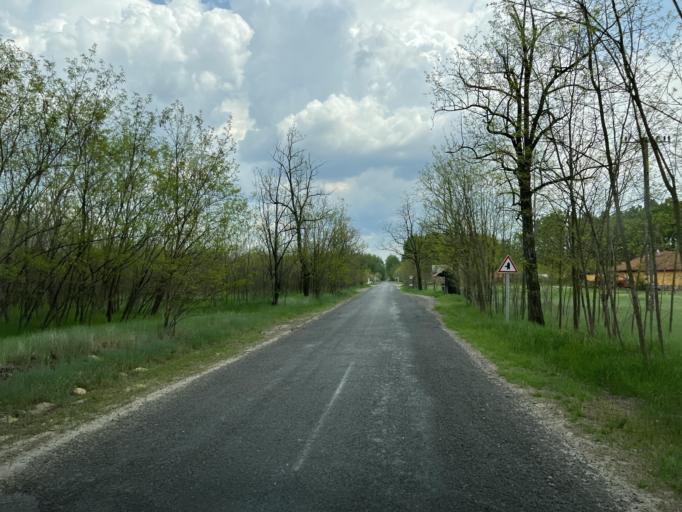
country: HU
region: Pest
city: Csemo
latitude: 47.1015
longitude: 19.7298
